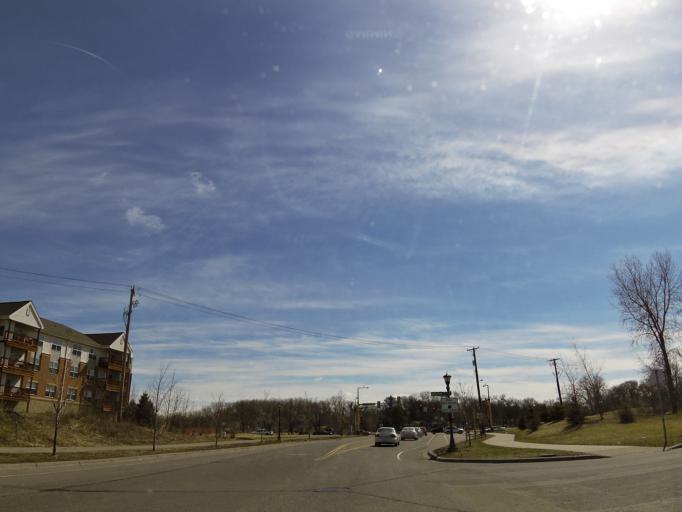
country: US
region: Minnesota
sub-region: Ramsey County
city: Maplewood
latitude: 44.9753
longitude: -93.0461
